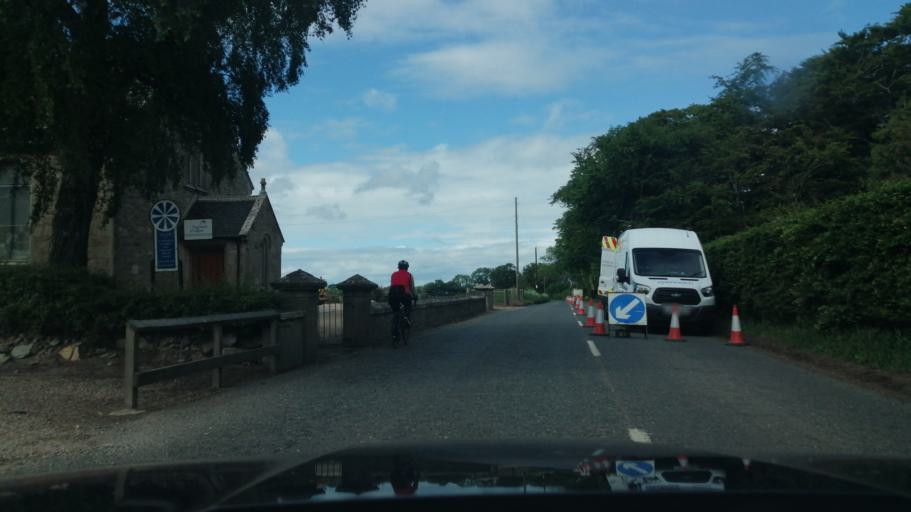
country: GB
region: Scotland
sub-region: Moray
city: Lhanbryd
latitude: 57.6424
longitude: -3.2475
